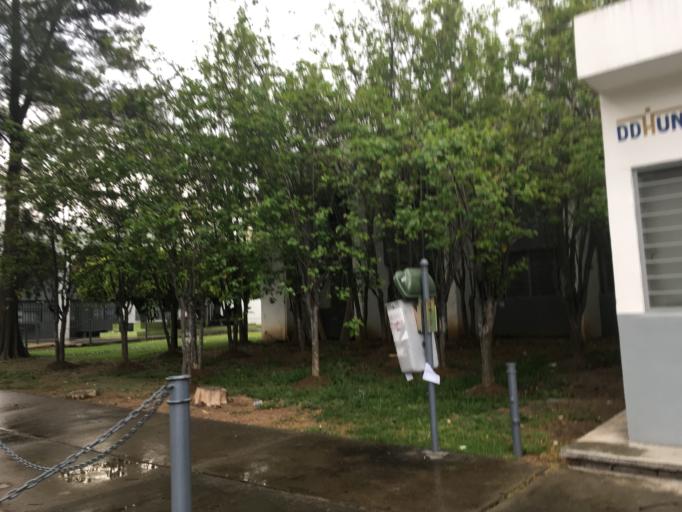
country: MX
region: Michoacan
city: Morelia
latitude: 19.6881
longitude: -101.2019
